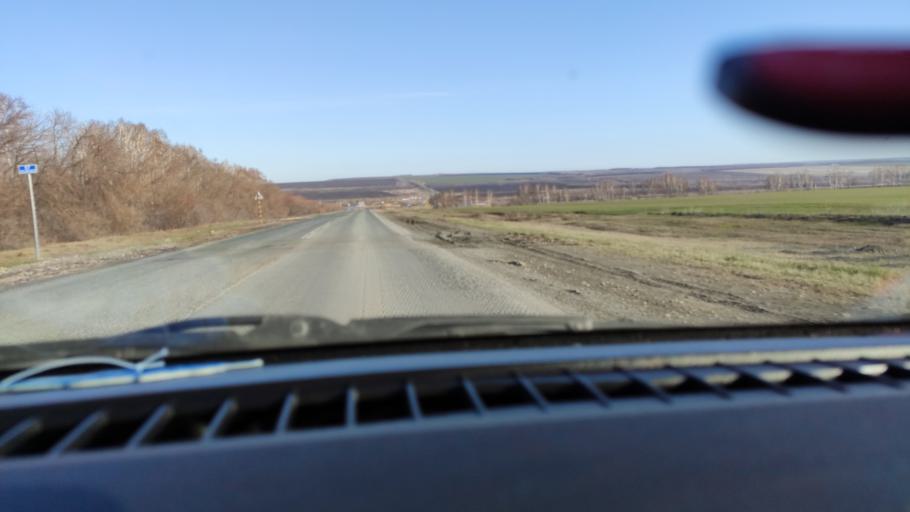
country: RU
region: Saratov
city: Dukhovnitskoye
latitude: 52.7245
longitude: 48.2614
